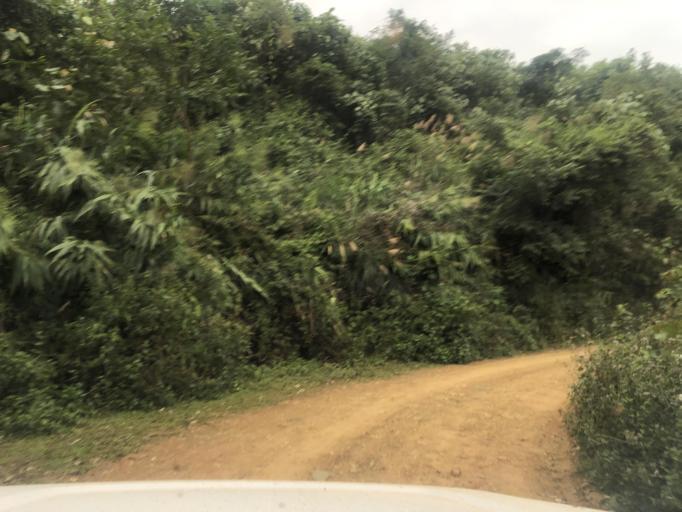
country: LA
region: Phongsali
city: Khoa
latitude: 21.2652
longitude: 102.5874
